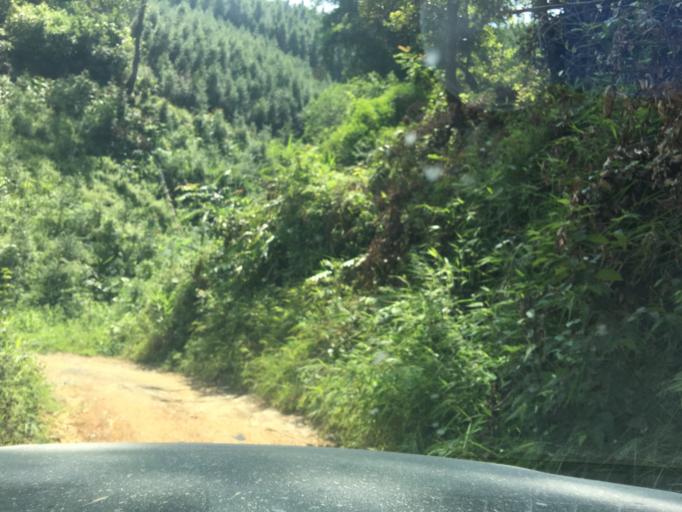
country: CN
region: Guangxi Zhuangzu Zizhiqu
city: Xinzhou
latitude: 25.0435
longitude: 105.8670
